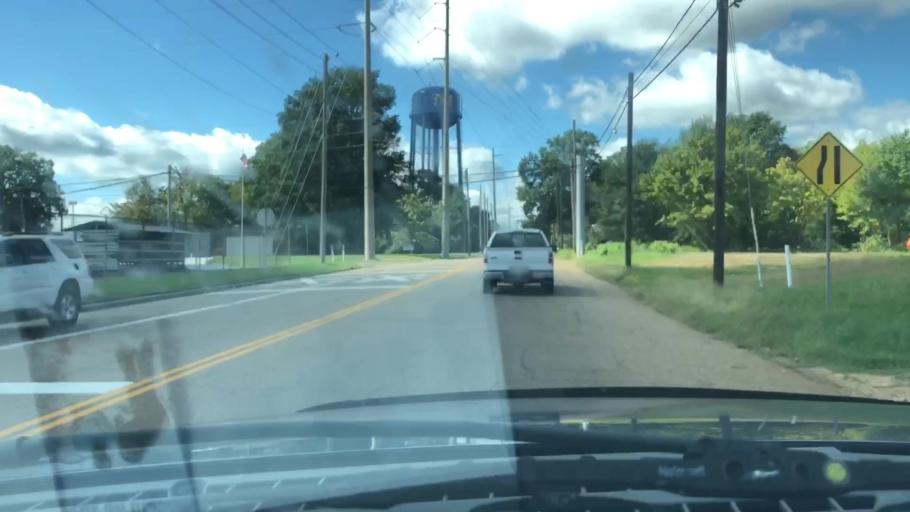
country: US
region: Texas
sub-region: Bowie County
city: Texarkana
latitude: 33.4195
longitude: -94.0529
